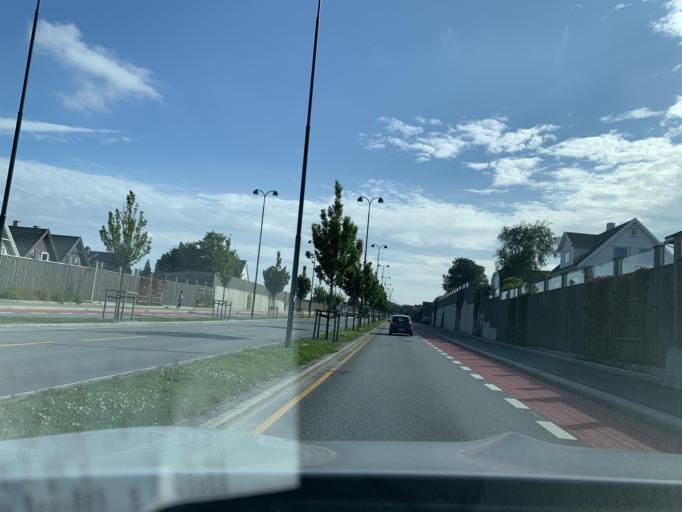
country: NO
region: Rogaland
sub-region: Stavanger
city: Stavanger
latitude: 58.9327
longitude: 5.7392
